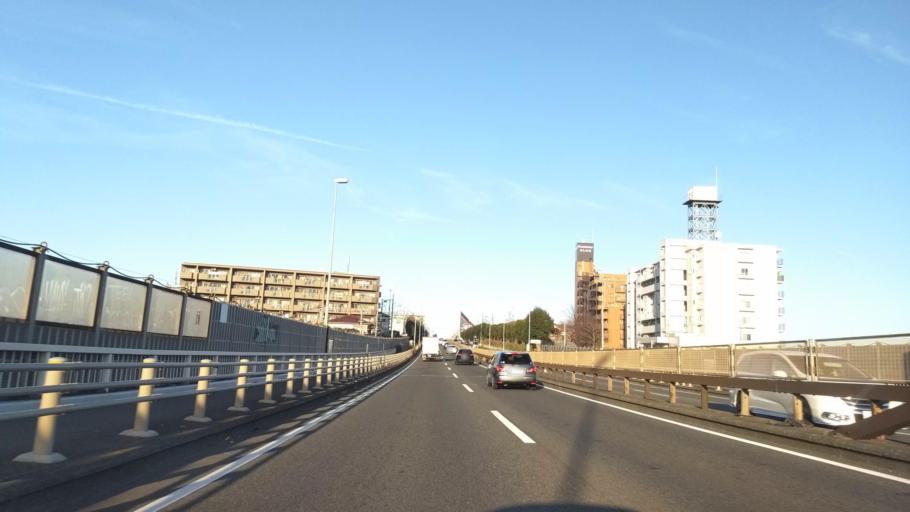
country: JP
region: Kanagawa
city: Zama
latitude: 35.4690
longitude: 139.4085
